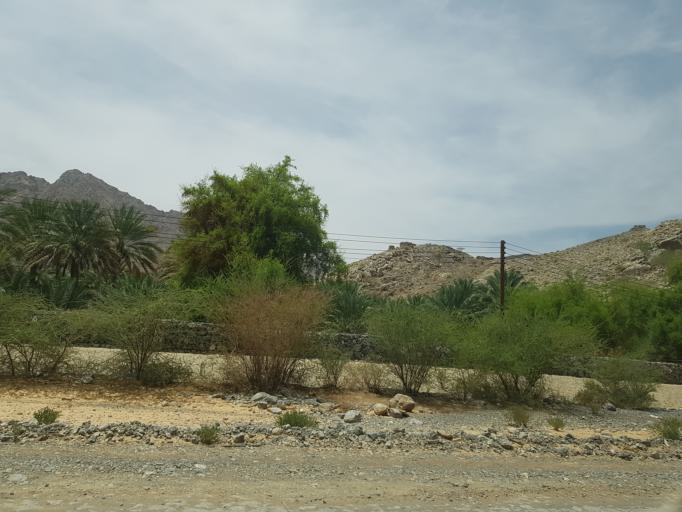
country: OM
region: Muhafazat ad Dakhiliyah
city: Izki
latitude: 22.9525
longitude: 57.6740
